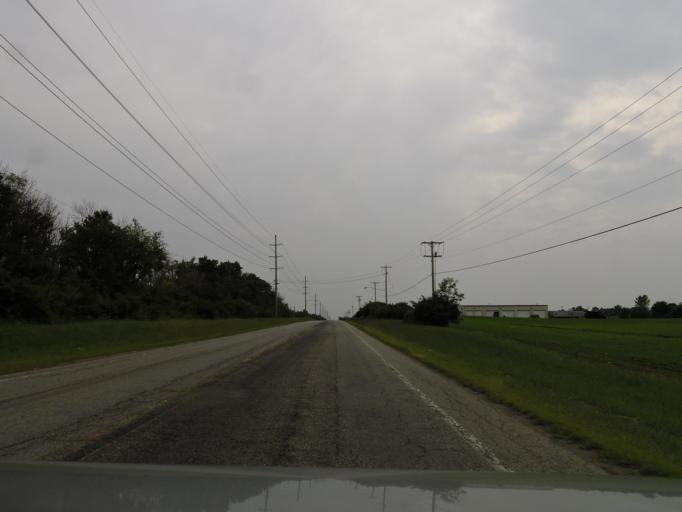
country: US
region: Ohio
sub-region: Clinton County
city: Wilmington
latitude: 39.4158
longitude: -83.8431
